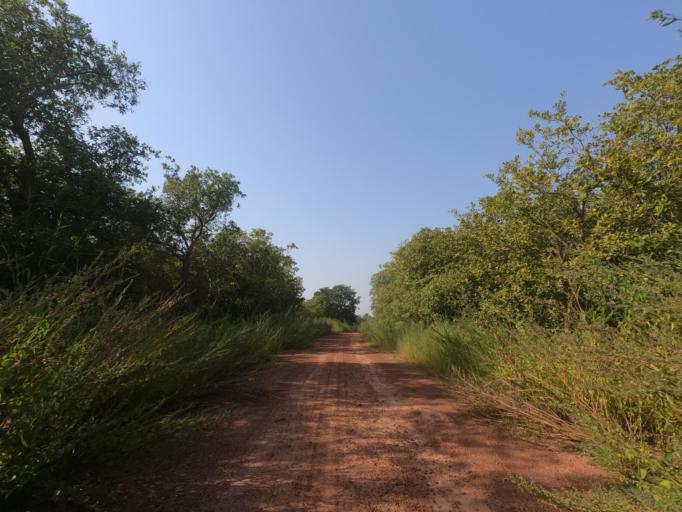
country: SN
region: Sedhiou
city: Sedhiou
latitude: 12.4418
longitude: -15.7384
